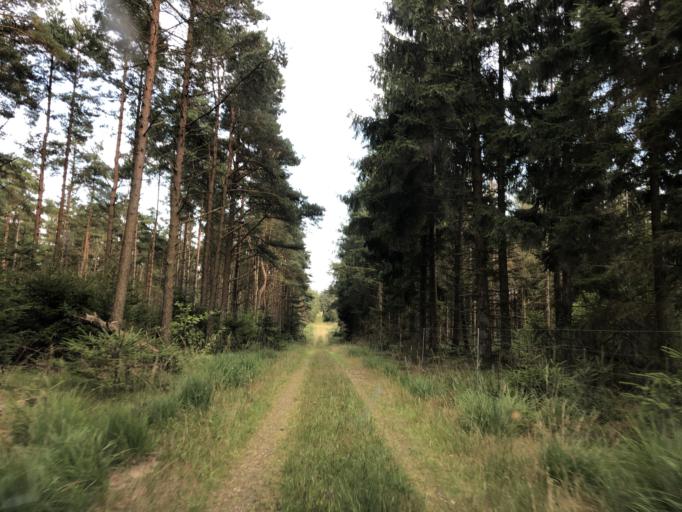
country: DK
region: Central Jutland
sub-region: Holstebro Kommune
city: Ulfborg
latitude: 56.2857
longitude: 8.4173
